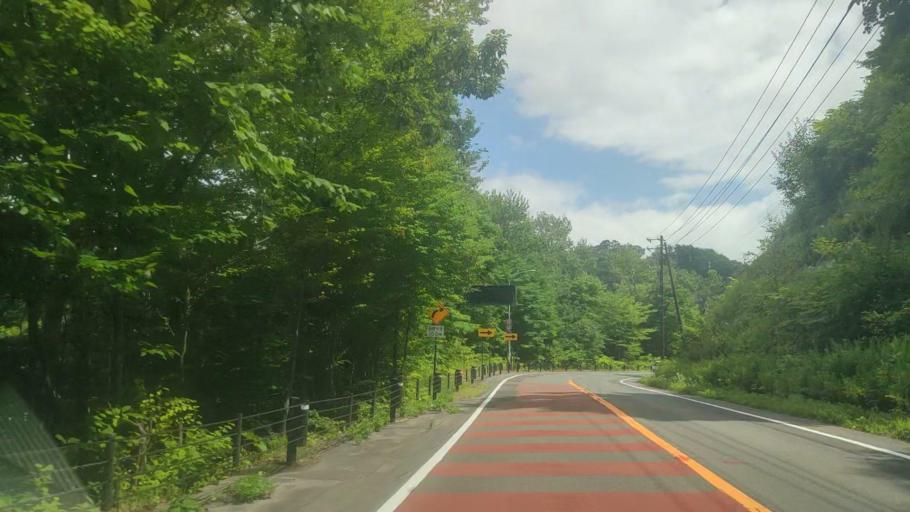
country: JP
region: Hokkaido
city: Date
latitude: 42.5646
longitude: 140.8825
